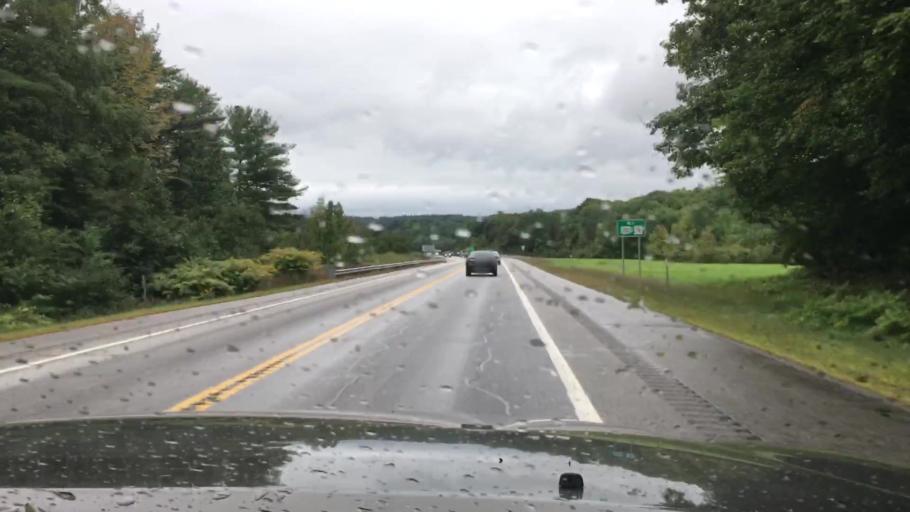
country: US
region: New Hampshire
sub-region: Merrimack County
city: Henniker
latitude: 43.1832
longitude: -71.8350
